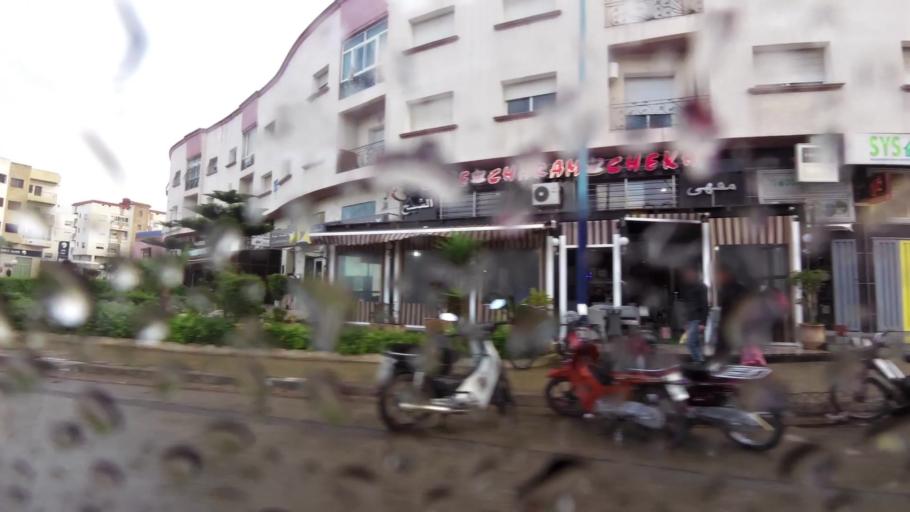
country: MA
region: Doukkala-Abda
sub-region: El-Jadida
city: El Jadida
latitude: 33.2361
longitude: -8.5244
